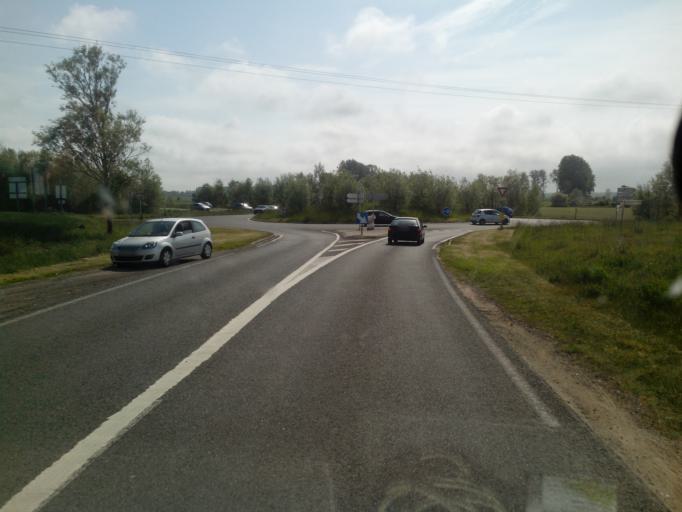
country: FR
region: Picardie
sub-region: Departement de la Somme
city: Quend
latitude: 50.3093
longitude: 1.6369
